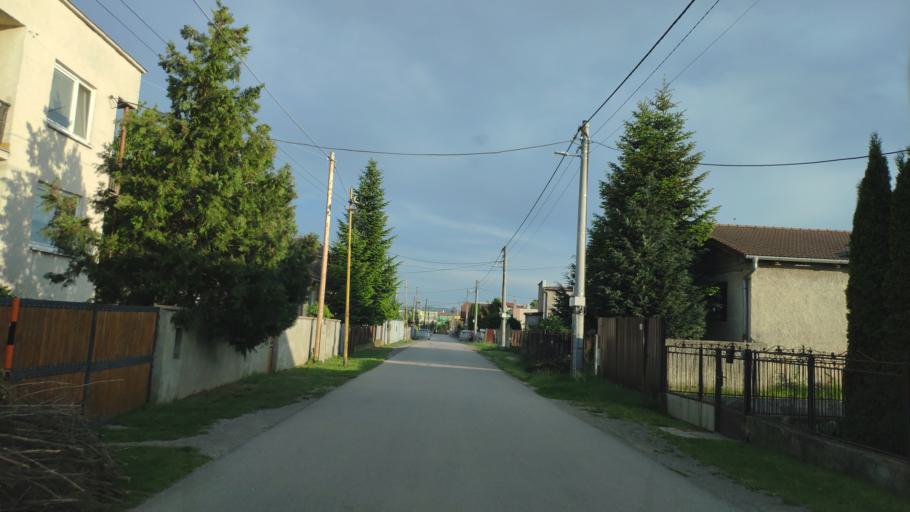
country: SK
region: Kosicky
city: Kosice
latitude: 48.6168
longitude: 21.3234
